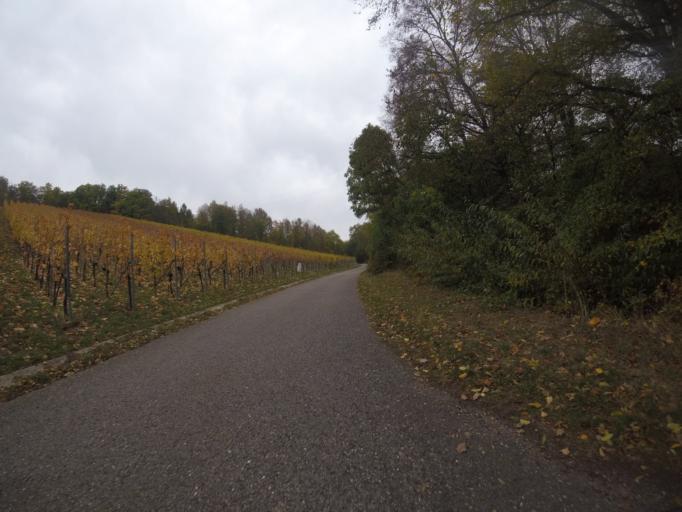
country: DE
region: Baden-Wuerttemberg
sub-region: Regierungsbezirk Stuttgart
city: Grossbottwar
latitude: 48.9928
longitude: 9.3199
